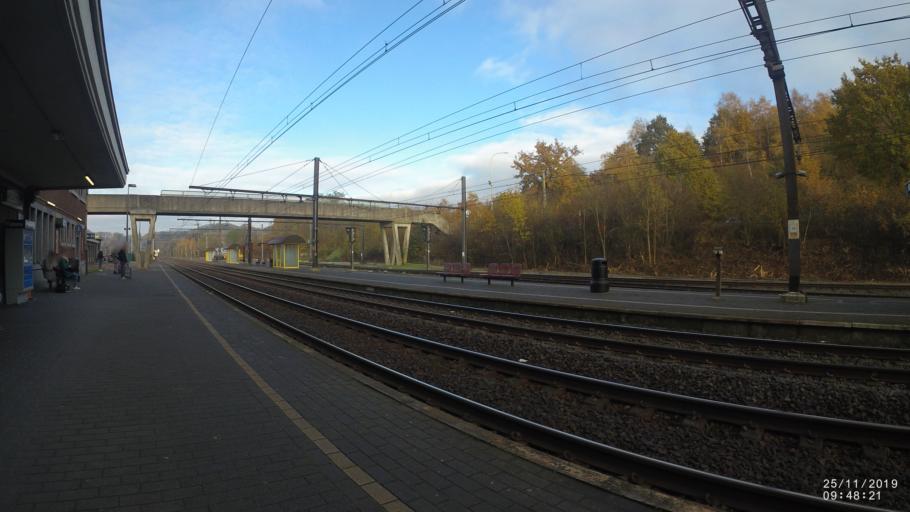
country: BE
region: Flanders
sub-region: Provincie Vlaams-Brabant
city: Diest
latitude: 50.9931
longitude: 5.0514
